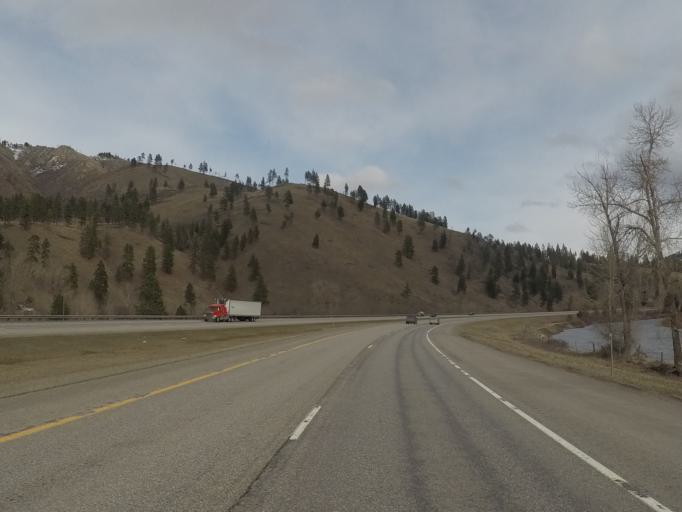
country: US
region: Montana
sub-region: Missoula County
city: Clinton
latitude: 46.7118
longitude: -113.5146
